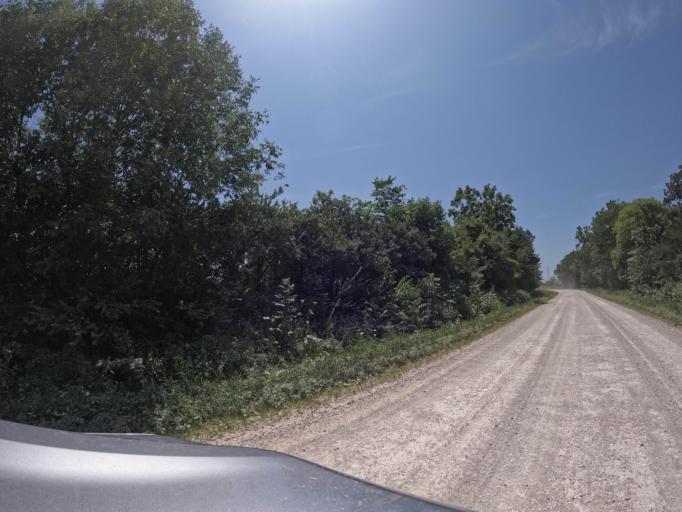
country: US
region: Iowa
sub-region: Henry County
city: Mount Pleasant
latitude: 40.9368
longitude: -91.5813
